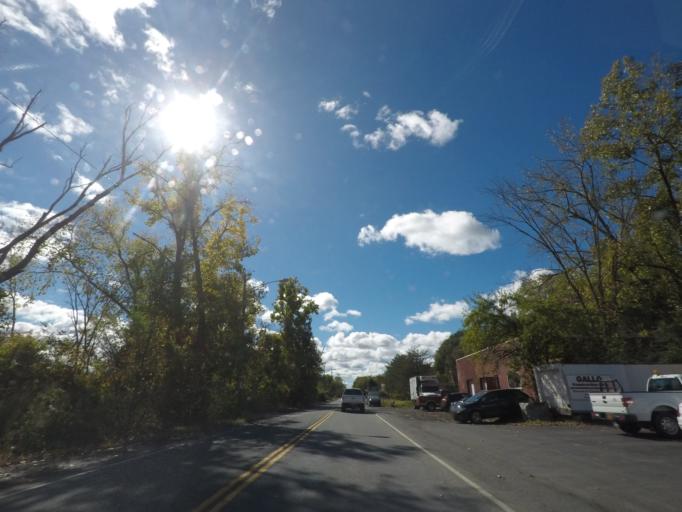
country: US
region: New York
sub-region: Albany County
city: Watervliet
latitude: 42.7190
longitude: -73.7168
